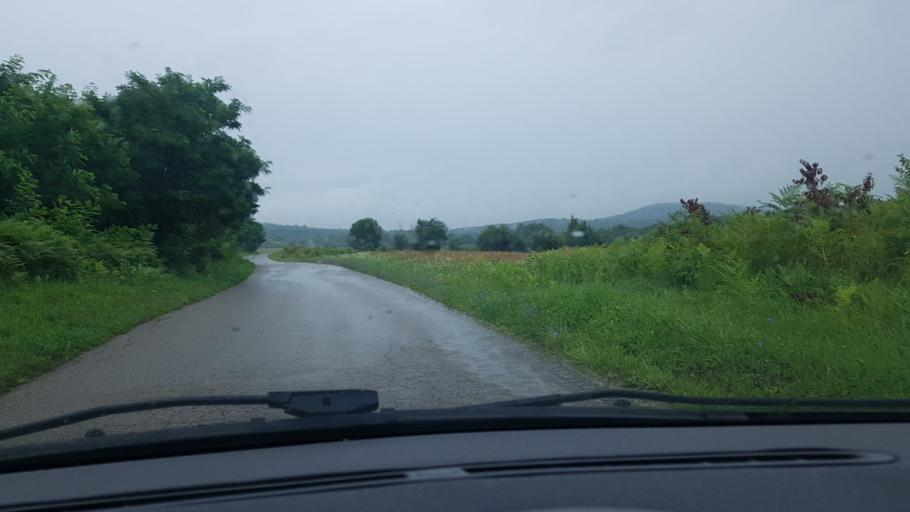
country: HR
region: Licko-Senjska
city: Jezerce
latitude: 44.9897
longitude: 15.6655
